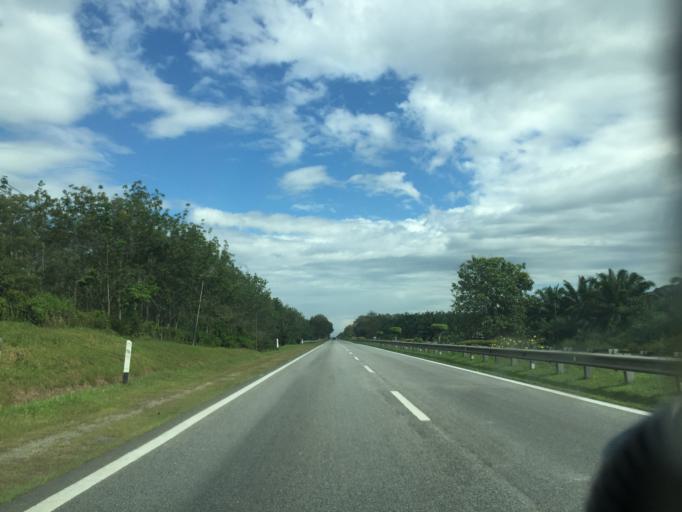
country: MY
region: Kedah
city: Jitra
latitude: 6.3795
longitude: 100.4244
